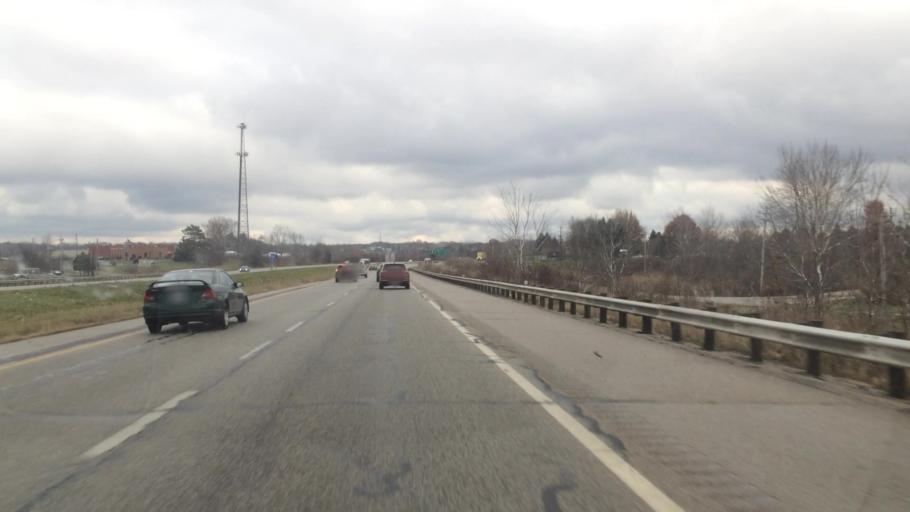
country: US
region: Ohio
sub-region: Portage County
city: Streetsboro
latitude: 41.2646
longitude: -81.3880
